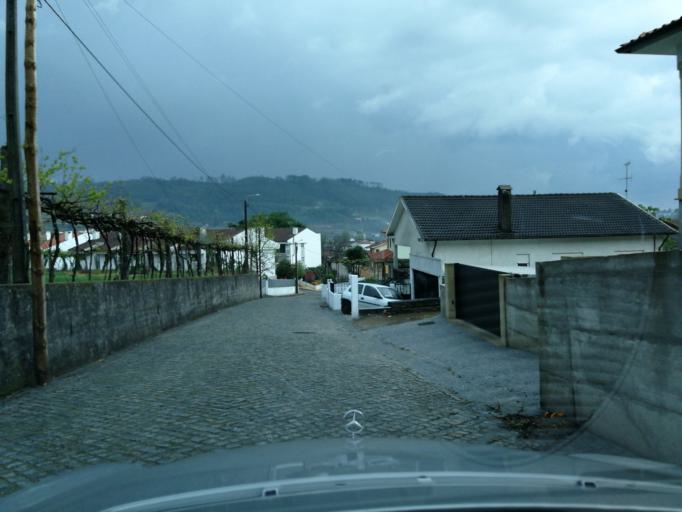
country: PT
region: Braga
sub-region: Braga
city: Oliveira
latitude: 41.4538
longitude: -8.4602
